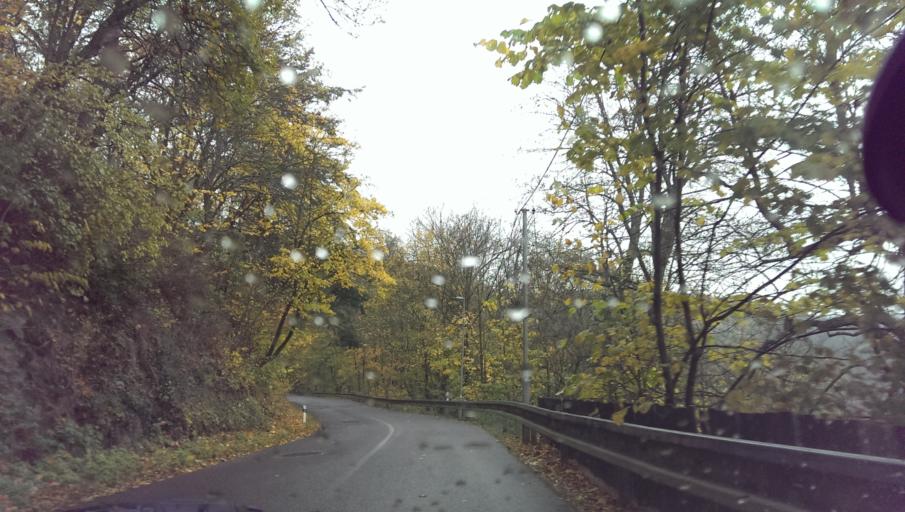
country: AT
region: Lower Austria
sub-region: Politischer Bezirk Hollabrunn
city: Hardegg
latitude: 48.8933
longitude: 15.8086
